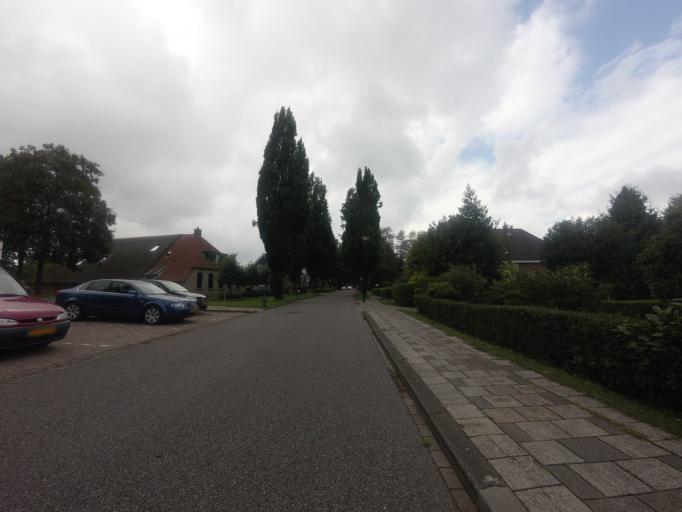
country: NL
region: Friesland
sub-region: Gemeente Skarsterlan
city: Oudehaske
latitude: 52.9321
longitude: 5.8569
